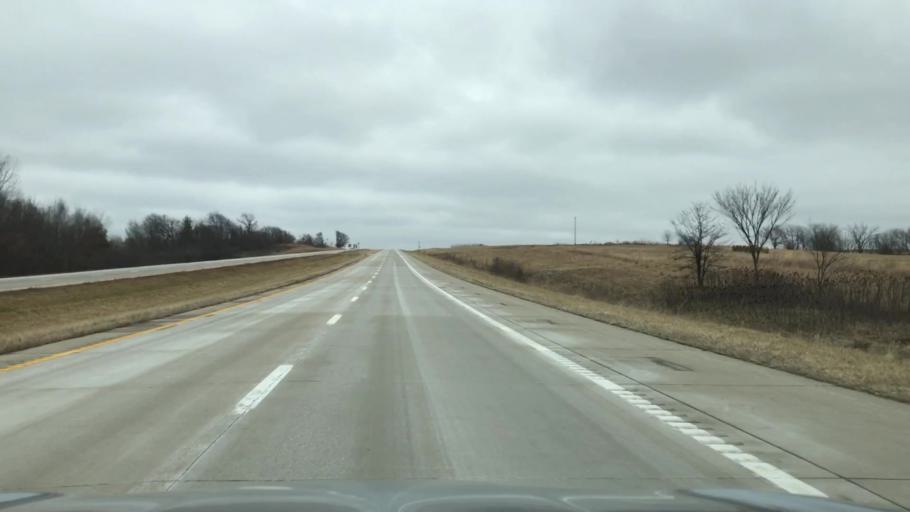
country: US
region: Missouri
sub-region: Livingston County
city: Chillicothe
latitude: 39.7380
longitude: -93.6979
